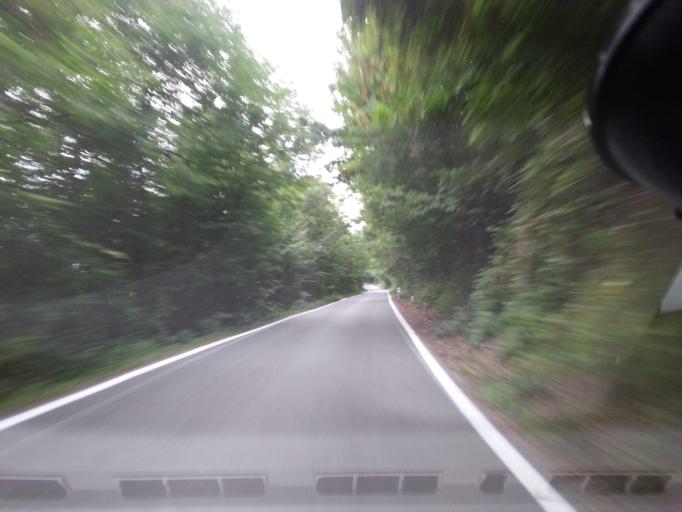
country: IT
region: Piedmont
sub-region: Provincia di Torino
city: Valgioie
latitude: 45.0717
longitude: 7.3622
